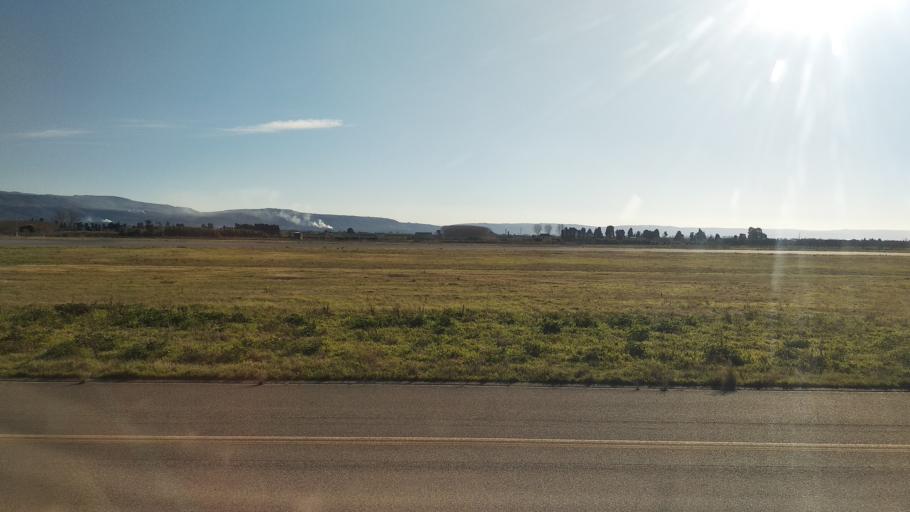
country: IT
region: Calabria
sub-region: Provincia di Catanzaro
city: Santa Eufemia Lamezia
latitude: 38.9070
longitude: 16.2479
